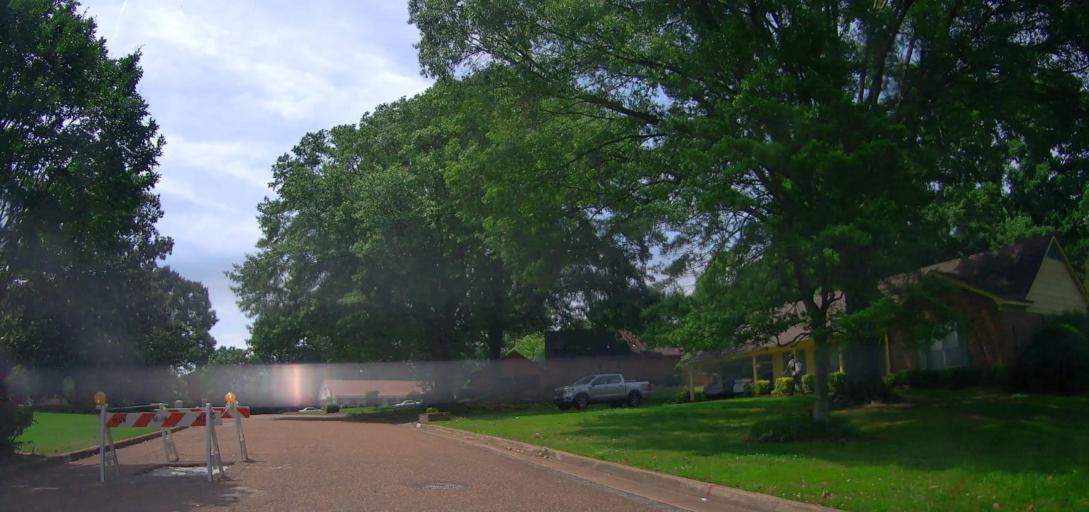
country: US
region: Tennessee
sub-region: Shelby County
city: Germantown
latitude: 35.0440
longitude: -89.7883
